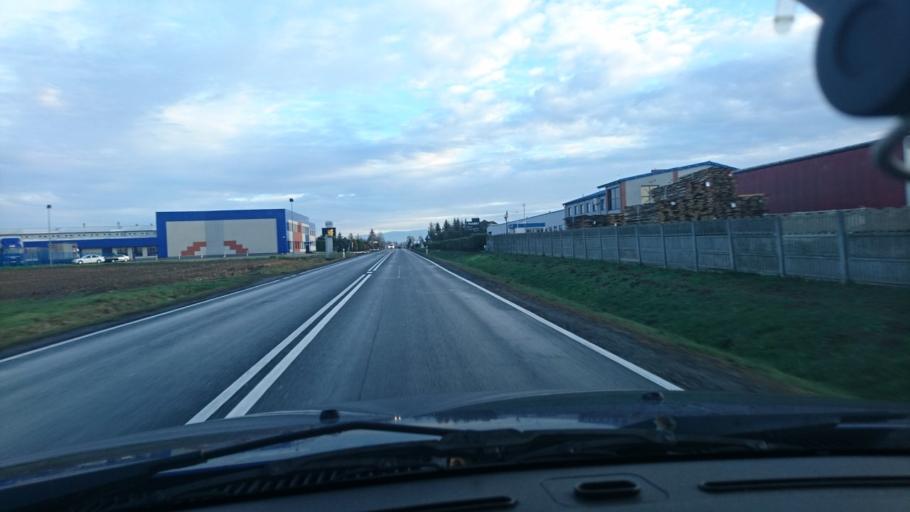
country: PL
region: Greater Poland Voivodeship
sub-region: Powiat kepinski
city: Leka Opatowska
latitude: 51.2296
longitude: 18.0777
